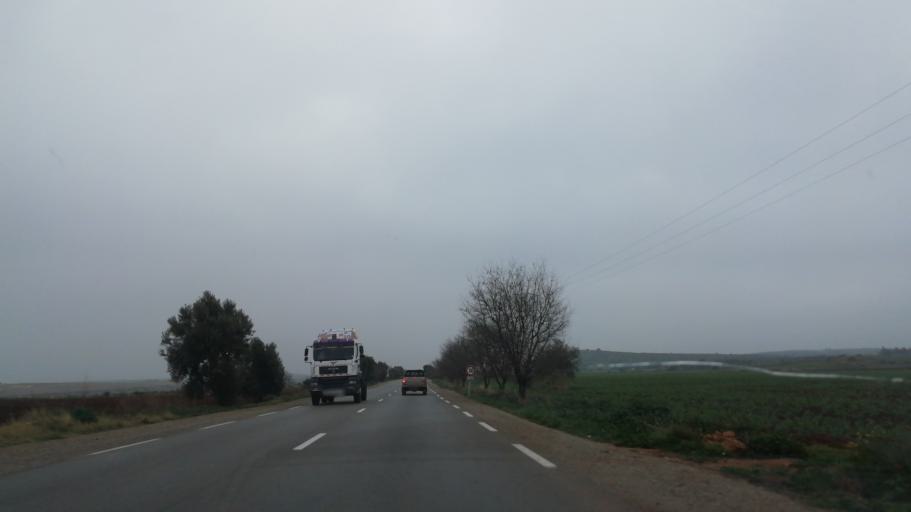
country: DZ
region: Mascara
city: Mascara
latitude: 35.3123
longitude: 0.3905
